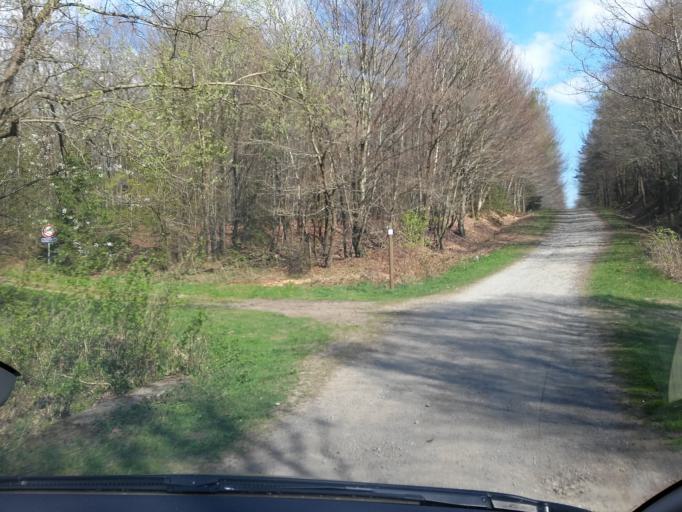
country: BE
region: Wallonia
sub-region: Province du Luxembourg
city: Habay-la-Vieille
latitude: 49.7346
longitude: 5.6601
